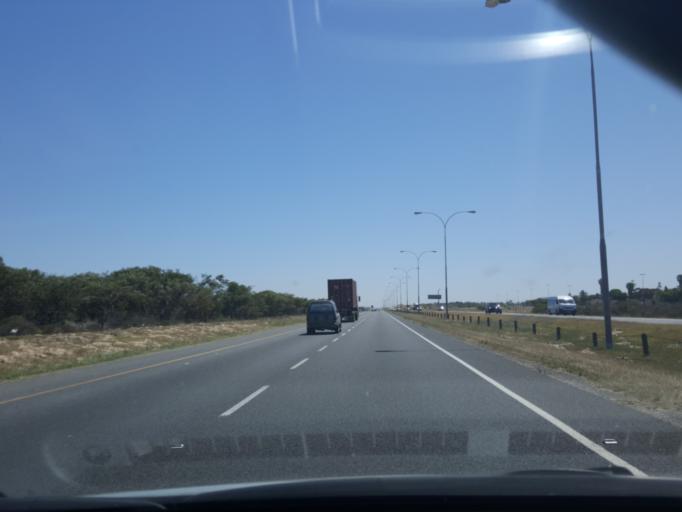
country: ZA
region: Western Cape
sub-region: City of Cape Town
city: Sunset Beach
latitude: -33.8338
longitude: 18.5382
